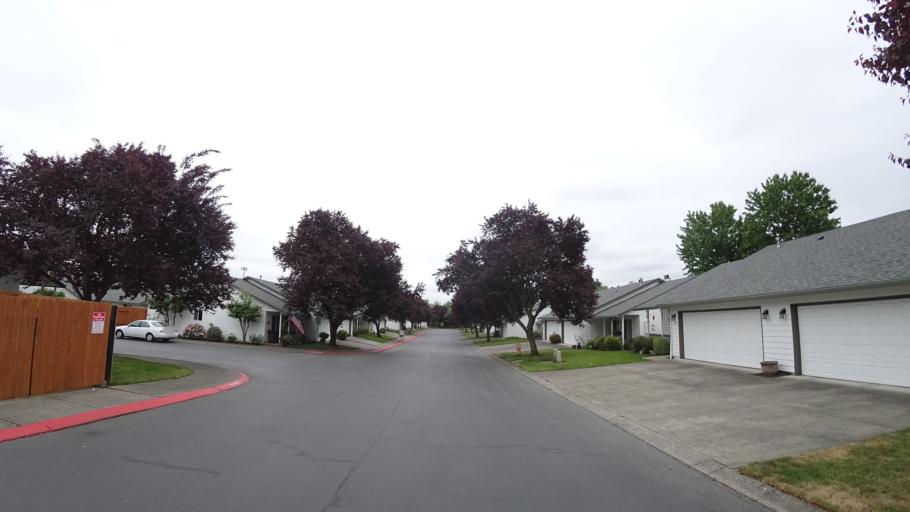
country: US
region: Oregon
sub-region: Washington County
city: Aloha
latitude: 45.5022
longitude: -122.9200
